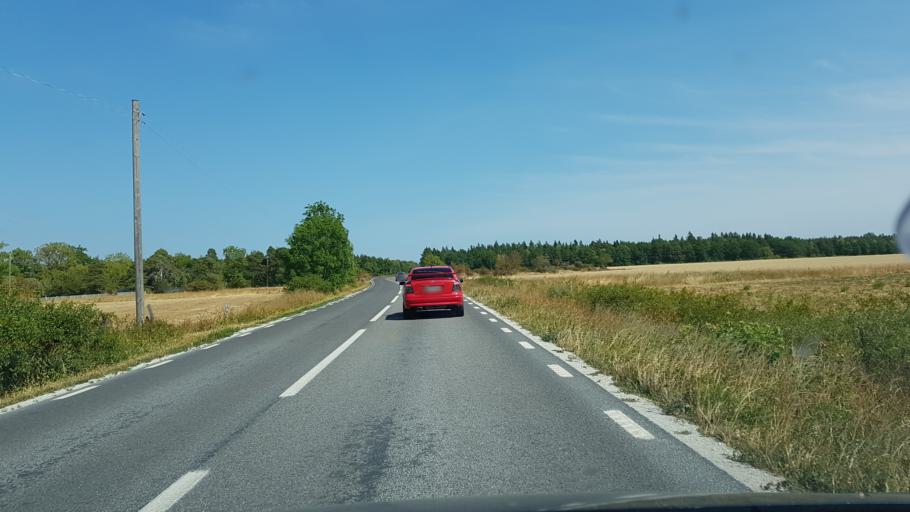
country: SE
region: Gotland
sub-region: Gotland
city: Visby
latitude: 57.6386
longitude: 18.4802
